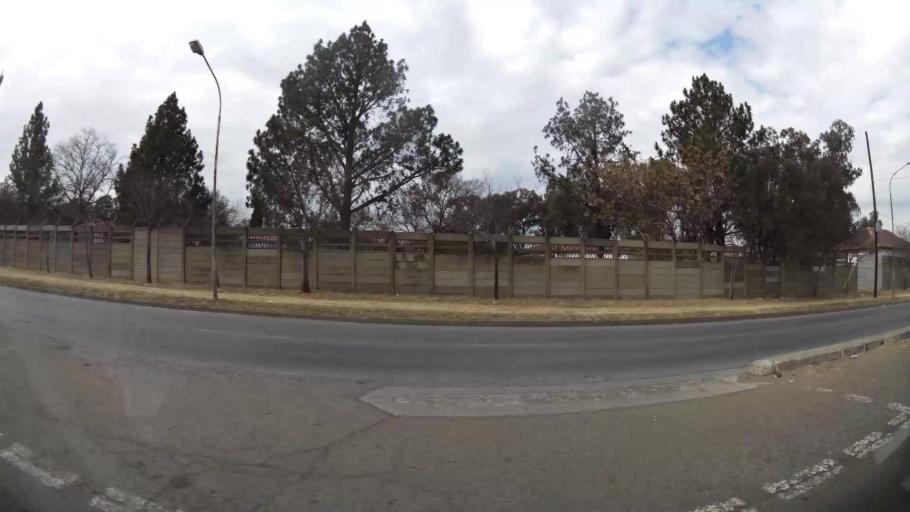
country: ZA
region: Orange Free State
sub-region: Fezile Dabi District Municipality
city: Kroonstad
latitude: -27.6539
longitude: 27.2308
